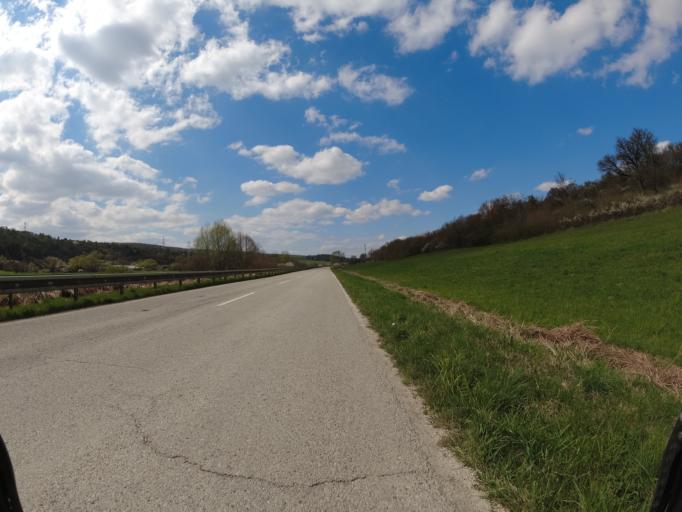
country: SK
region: Nitriansky
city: Cachtice
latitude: 48.7182
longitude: 17.7238
